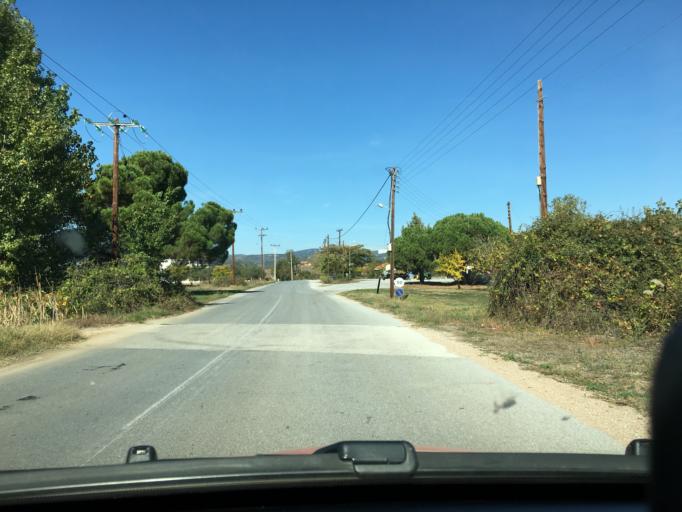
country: GR
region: Central Macedonia
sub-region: Nomos Chalkidikis
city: Megali Panagia
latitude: 40.3644
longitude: 23.7003
